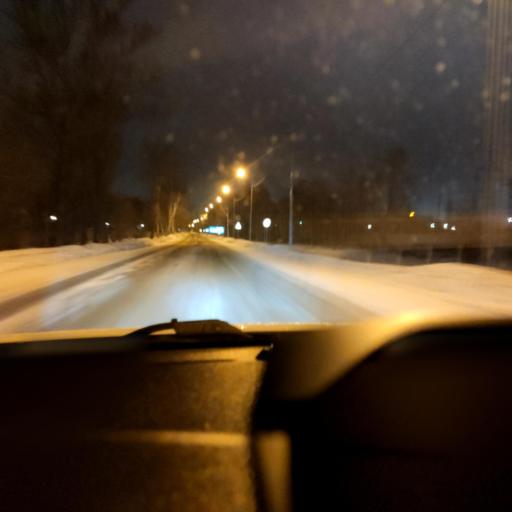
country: RU
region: Tatarstan
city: Vysokaya Gora
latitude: 55.8882
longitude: 49.2433
